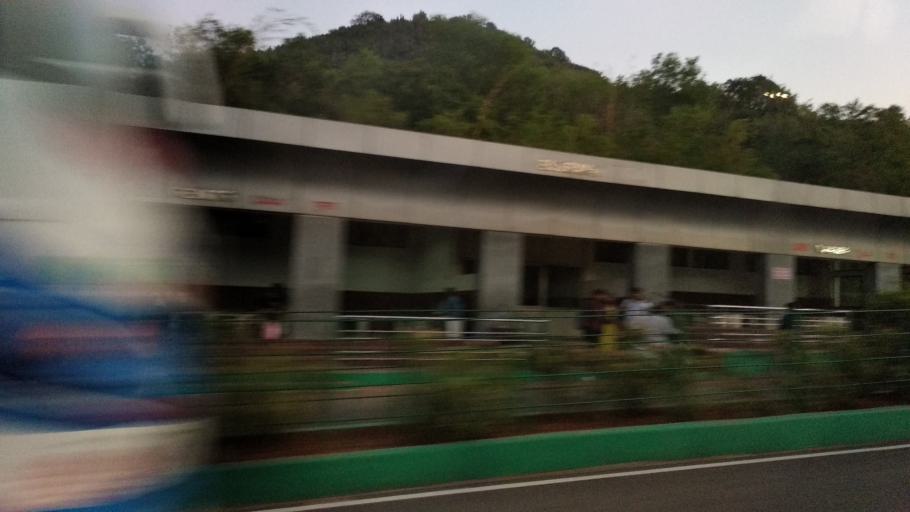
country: IN
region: Andhra Pradesh
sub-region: Vishakhapatnam
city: Bhimunipatnam
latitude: 17.7814
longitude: 83.3812
